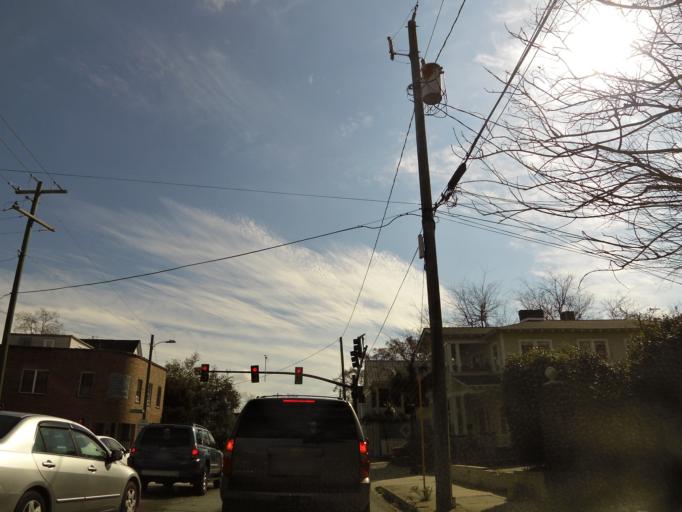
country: US
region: South Carolina
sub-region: Charleston County
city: Charleston
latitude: 32.7939
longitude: -79.9491
